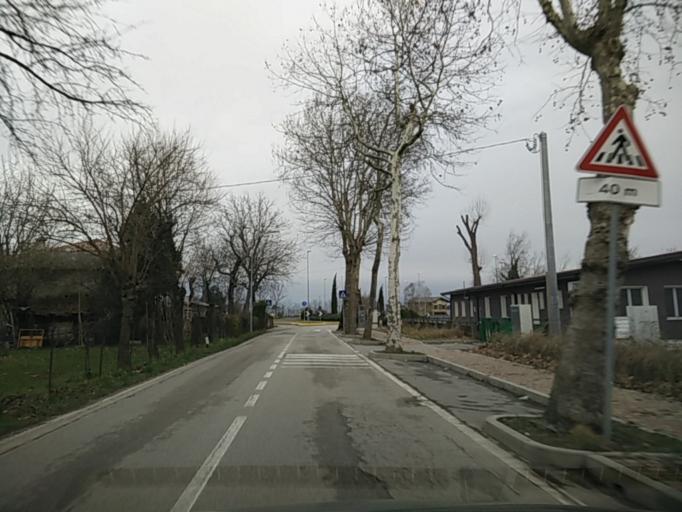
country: IT
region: Veneto
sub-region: Provincia di Treviso
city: Caselle
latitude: 45.7438
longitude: 12.0092
